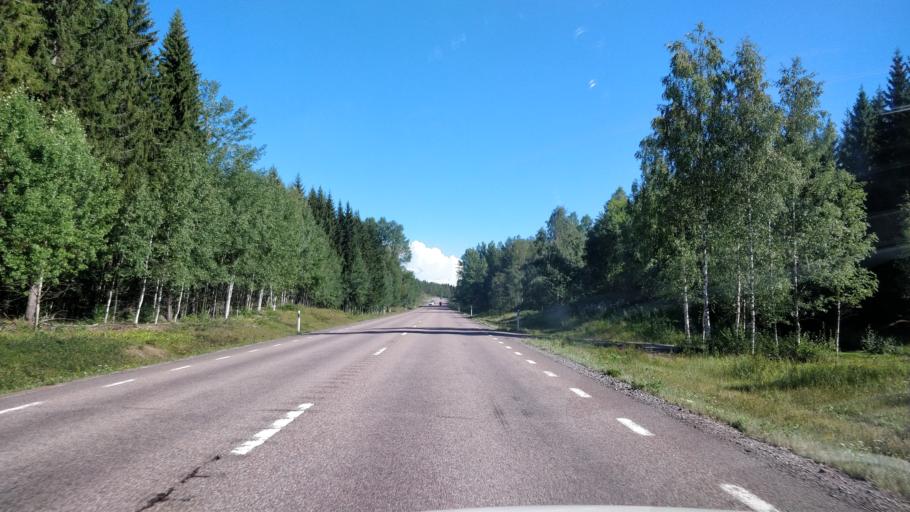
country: SE
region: Dalarna
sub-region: Faluns Kommun
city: Falun
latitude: 60.6508
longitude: 15.5610
